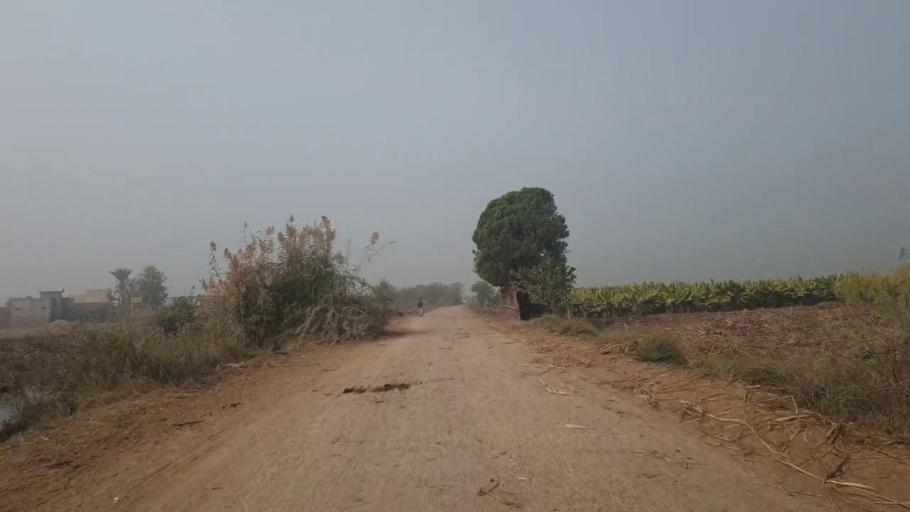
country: PK
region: Sindh
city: Tando Adam
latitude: 25.8089
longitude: 68.5842
